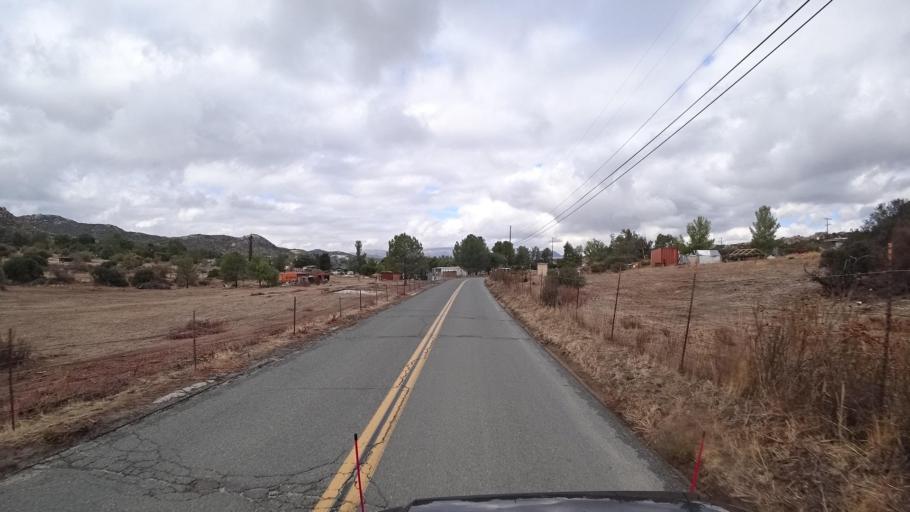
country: US
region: California
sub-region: San Diego County
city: Campo
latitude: 32.6299
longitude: -116.4259
